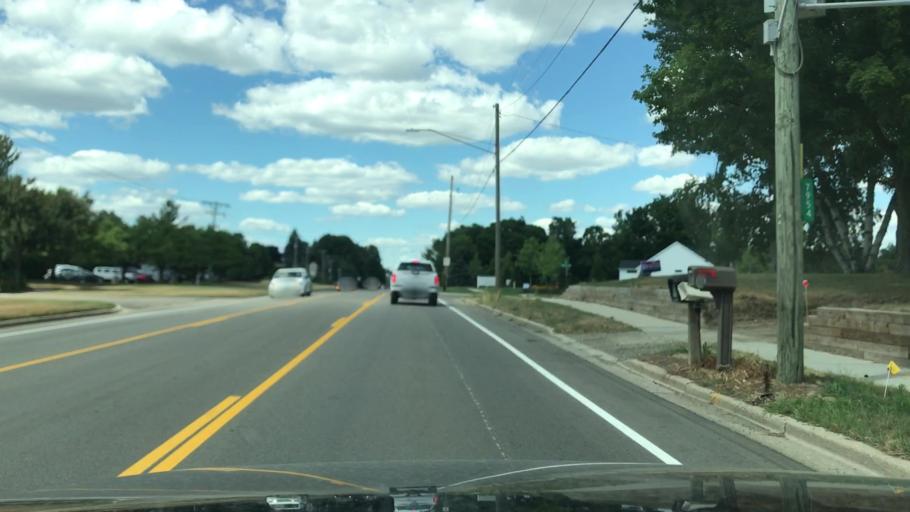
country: US
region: Michigan
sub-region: Kent County
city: Byron Center
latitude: 42.8201
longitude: -85.7230
